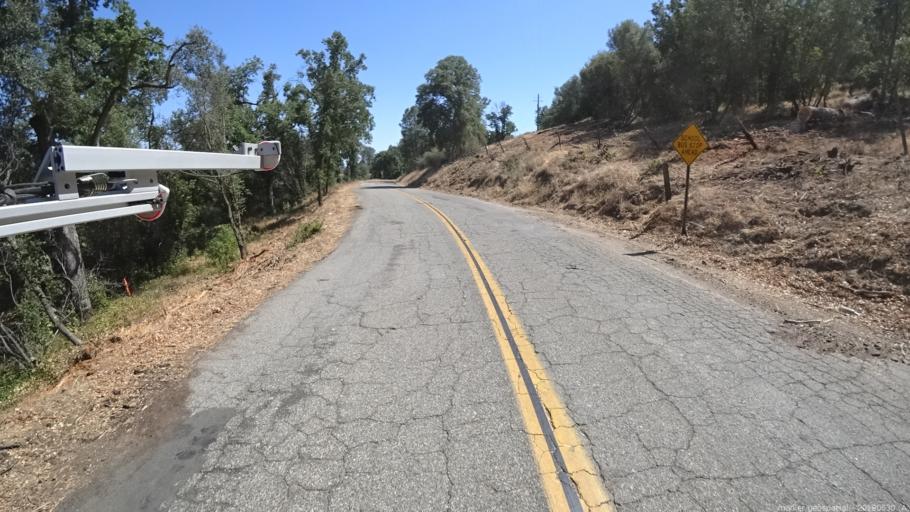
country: US
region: California
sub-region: Fresno County
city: Auberry
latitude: 37.2033
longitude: -119.4987
